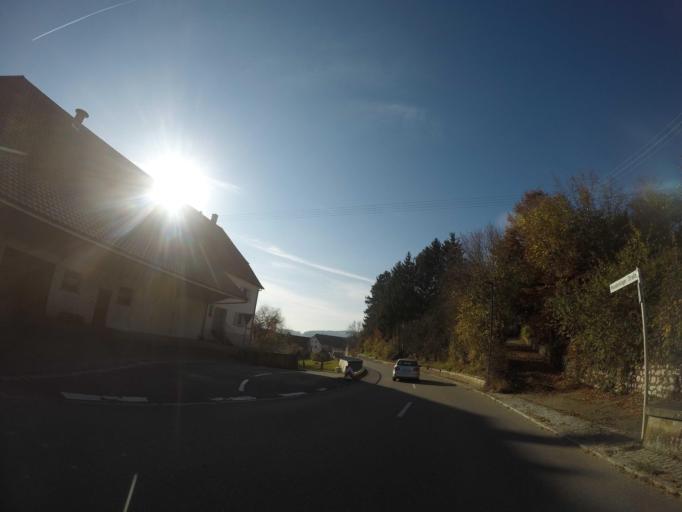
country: DE
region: Baden-Wuerttemberg
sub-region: Tuebingen Region
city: Hausen am Bussen
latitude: 48.2130
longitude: 9.6275
